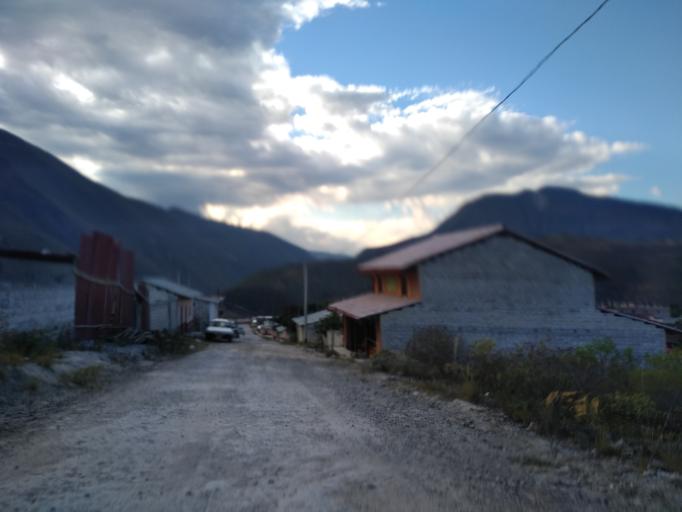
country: PE
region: Amazonas
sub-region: Provincia de Luya
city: Tingo
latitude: -6.3754
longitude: -77.9097
